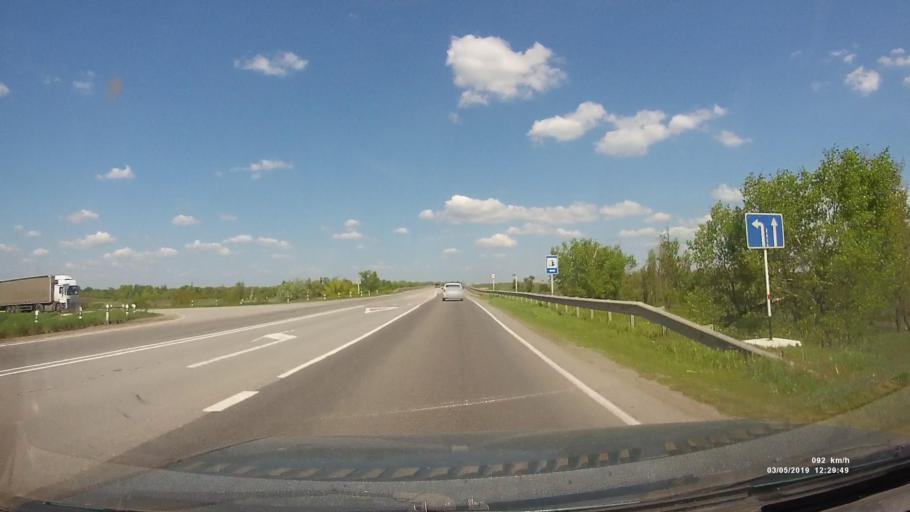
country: RU
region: Rostov
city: Semikarakorsk
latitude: 47.4929
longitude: 40.7385
